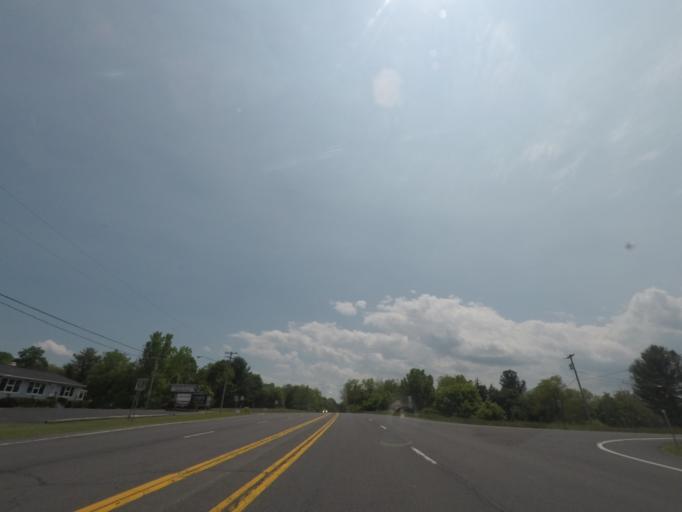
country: US
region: New York
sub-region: Columbia County
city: Kinderhook
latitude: 42.3923
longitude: -73.6880
